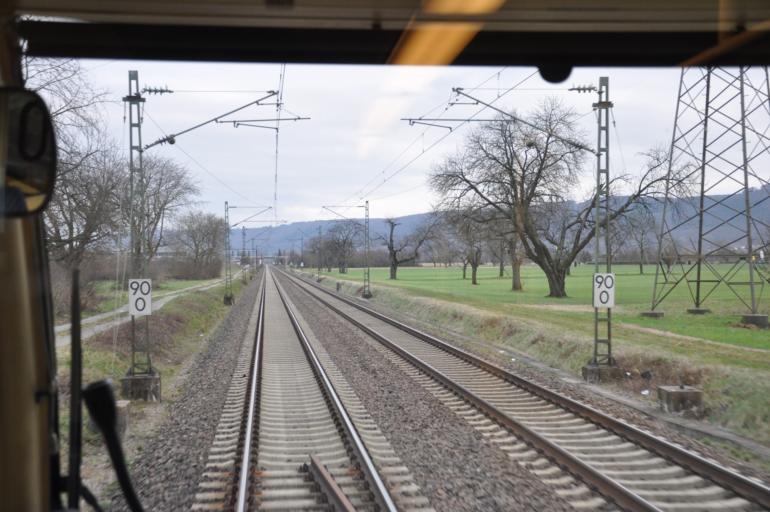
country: DE
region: Baden-Wuerttemberg
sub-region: Karlsruhe Region
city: Muggensturm
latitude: 48.8825
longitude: 8.2966
